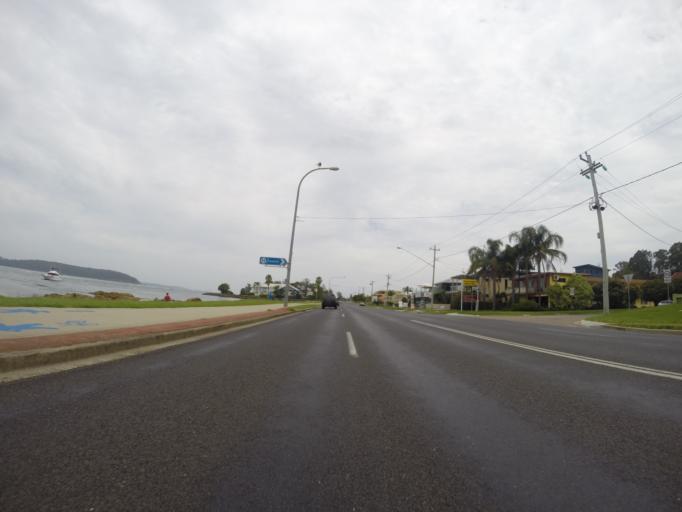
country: AU
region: New South Wales
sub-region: Eurobodalla
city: Batemans Bay
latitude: -35.7105
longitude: 150.1820
